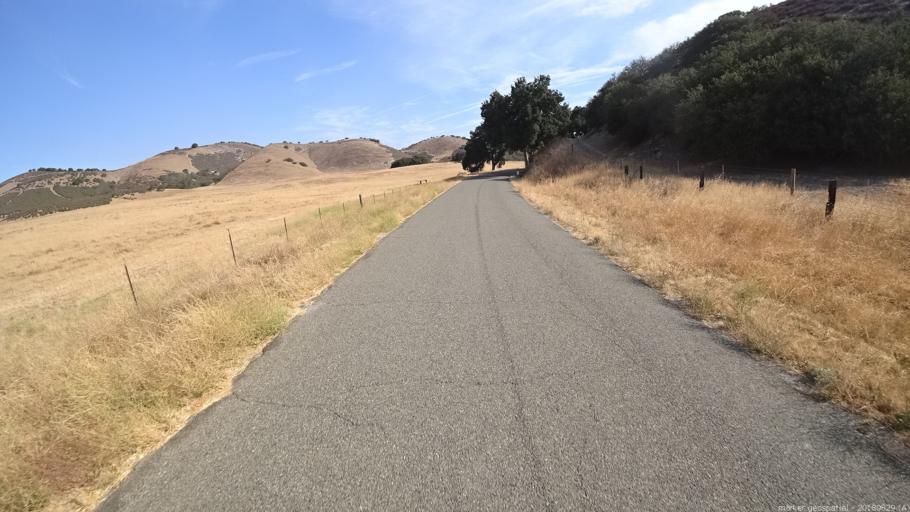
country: US
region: California
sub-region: Monterey County
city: King City
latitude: 36.0548
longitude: -121.0528
